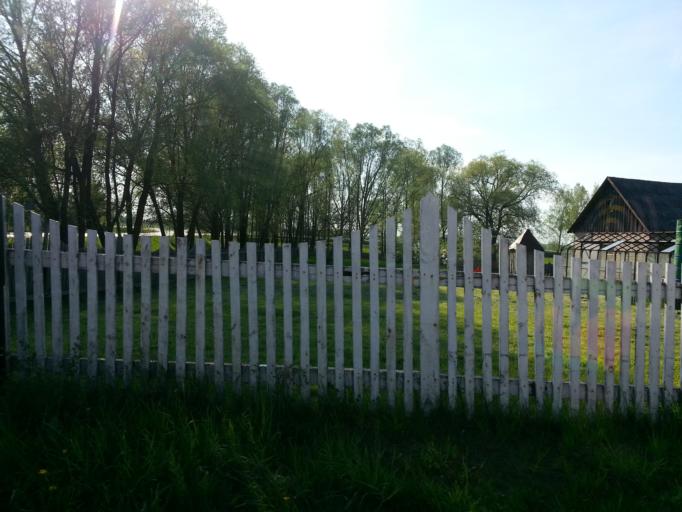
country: LT
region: Panevezys
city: Pasvalys
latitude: 55.9288
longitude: 24.3380
